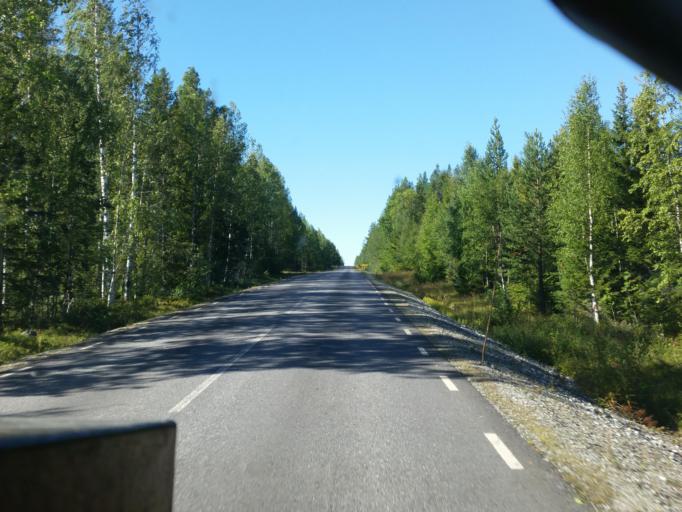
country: SE
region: Norrbotten
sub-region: Pitea Kommun
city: Roknas
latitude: 65.2138
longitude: 21.2345
